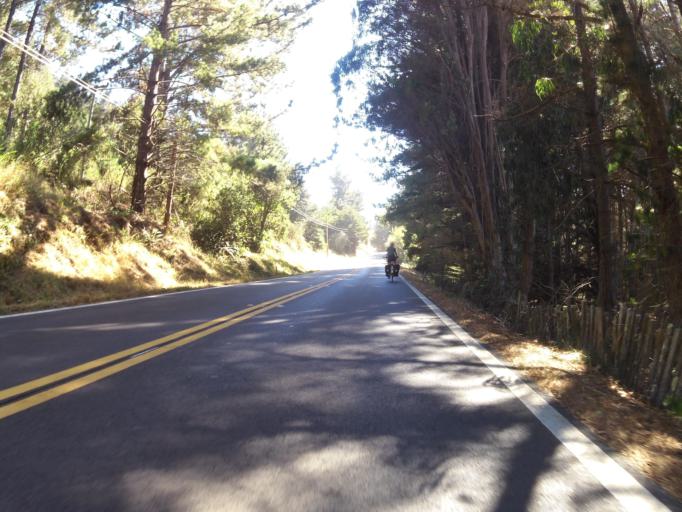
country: US
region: California
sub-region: Mendocino County
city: Fort Bragg
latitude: 39.6323
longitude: -123.7825
